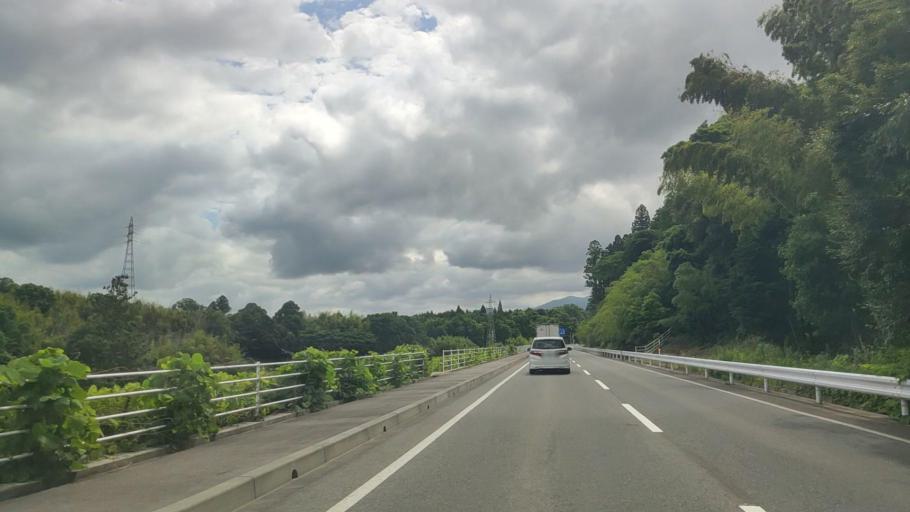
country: JP
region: Tottori
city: Yonago
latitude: 35.3765
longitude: 133.3999
